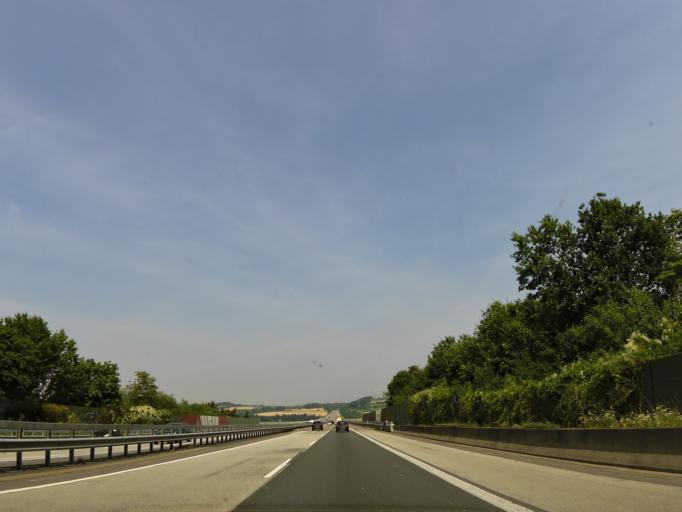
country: DE
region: Rheinland-Pfalz
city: Konigsfeld
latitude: 50.5394
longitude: 7.1682
